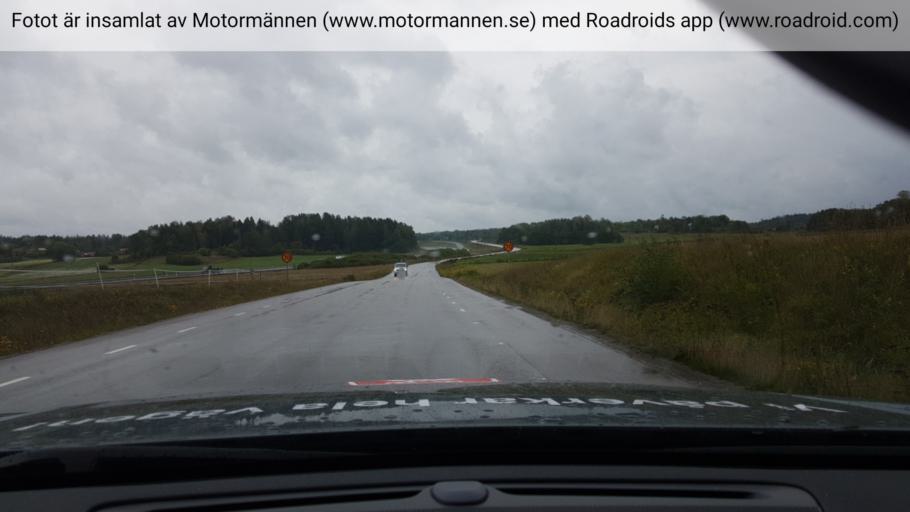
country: SE
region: Stockholm
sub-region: Haninge Kommun
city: Jordbro
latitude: 59.0625
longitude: 18.0499
